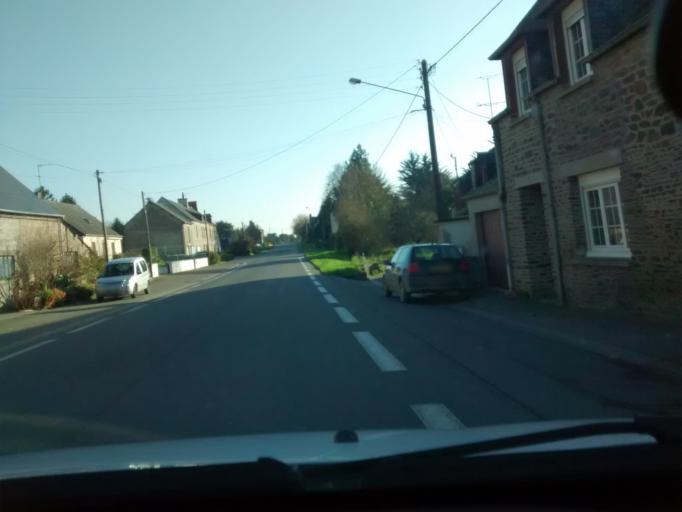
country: FR
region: Lower Normandy
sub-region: Departement de la Manche
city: Pontorson
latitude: 48.5407
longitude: -1.4946
